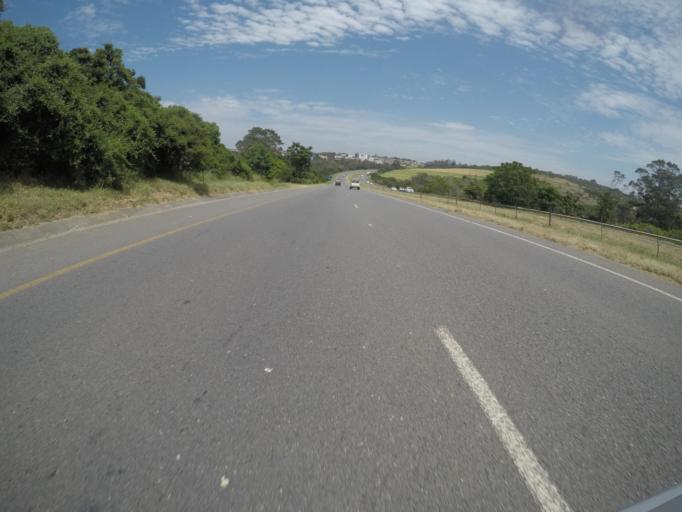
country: ZA
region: Eastern Cape
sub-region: Buffalo City Metropolitan Municipality
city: East London
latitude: -32.9429
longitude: 27.9431
